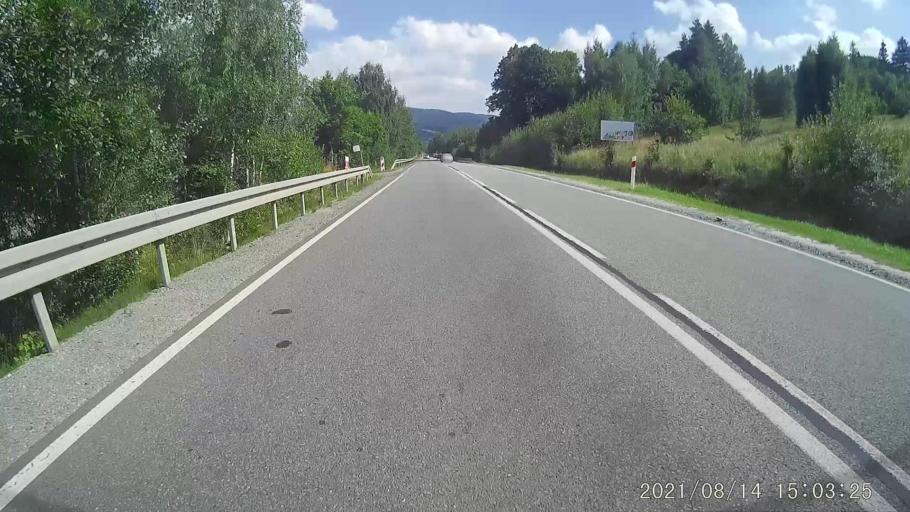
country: PL
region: Lower Silesian Voivodeship
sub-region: Powiat walbrzyski
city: Jedlina-Zdroj
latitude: 50.7250
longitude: 16.3274
